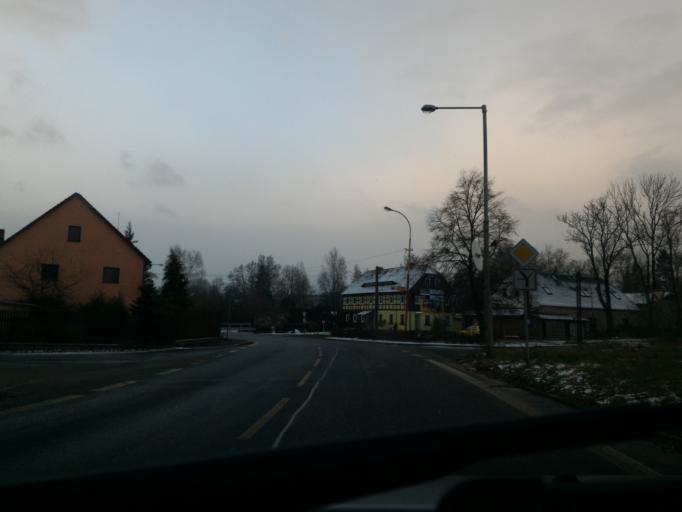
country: CZ
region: Ustecky
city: Varnsdorf
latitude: 50.9174
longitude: 14.6069
